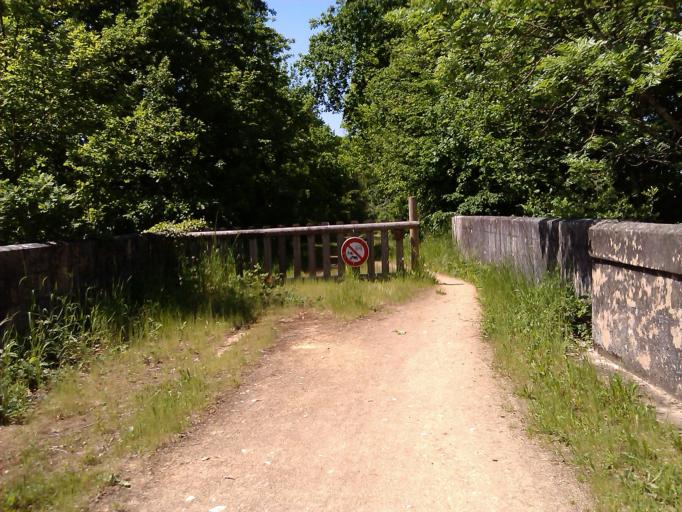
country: FR
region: Centre
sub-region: Departement de l'Indre
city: Saint-Marcel
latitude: 46.6237
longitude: 1.4718
